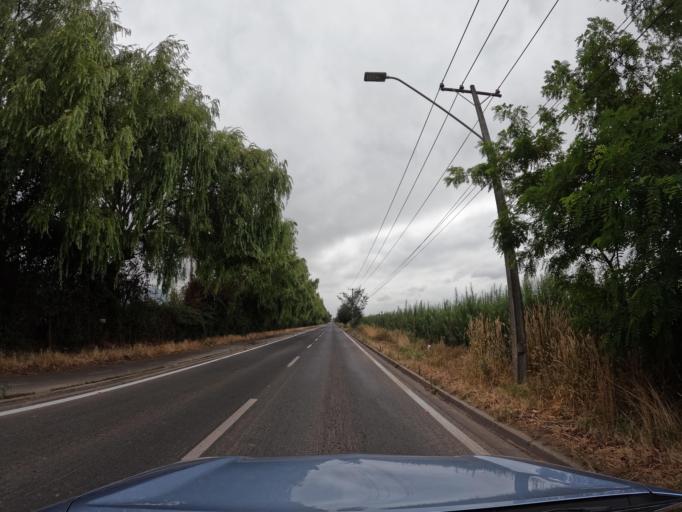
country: CL
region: O'Higgins
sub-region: Provincia de Colchagua
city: Chimbarongo
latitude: -34.7304
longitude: -71.0598
